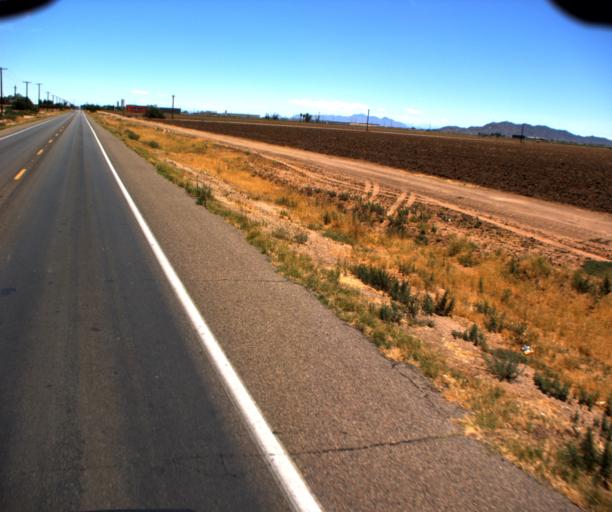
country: US
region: Arizona
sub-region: Pinal County
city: Casa Grande
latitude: 32.8794
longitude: -111.8030
